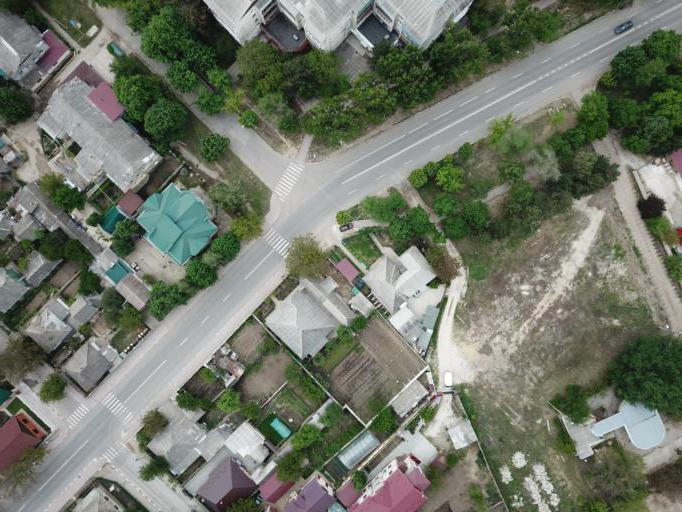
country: MD
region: Ungheni
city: Ungheni
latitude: 47.2183
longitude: 27.8021
